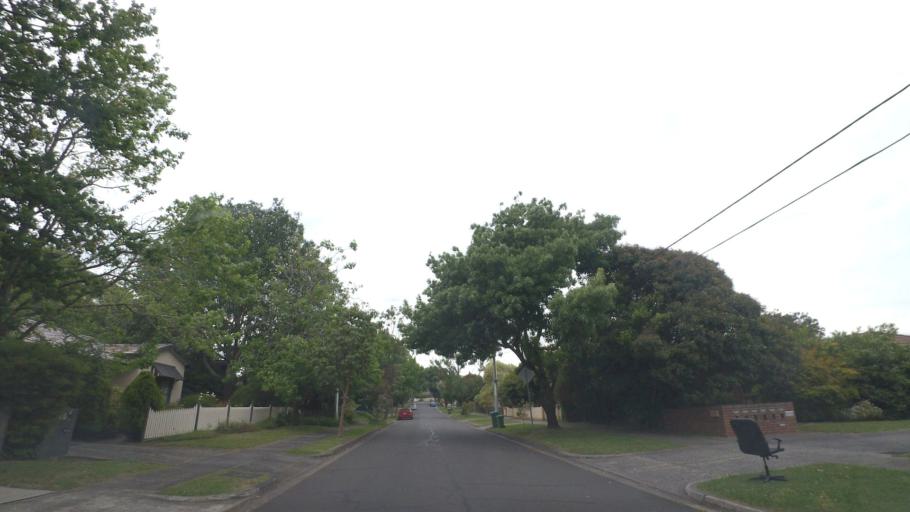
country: AU
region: Victoria
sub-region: Maroondah
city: Croydon North
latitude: -37.7935
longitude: 145.2886
